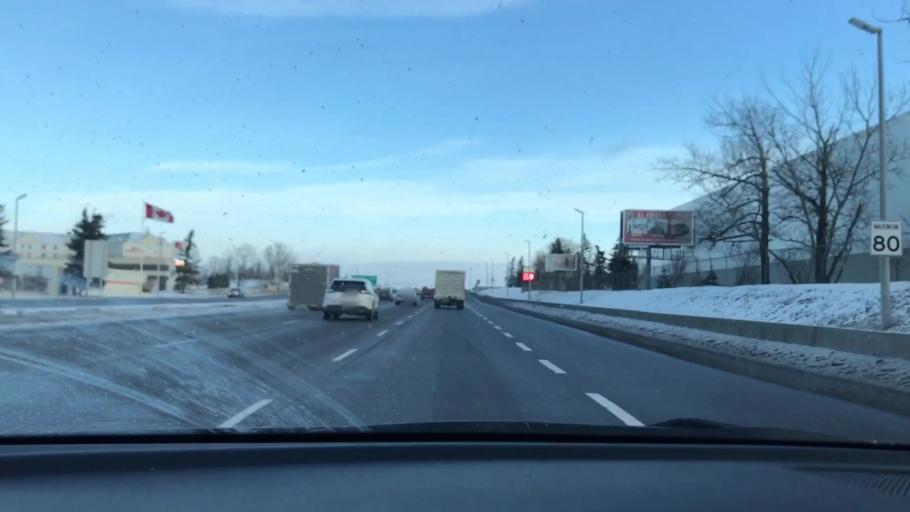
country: CA
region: Alberta
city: Calgary
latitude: 51.0927
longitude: -114.0090
